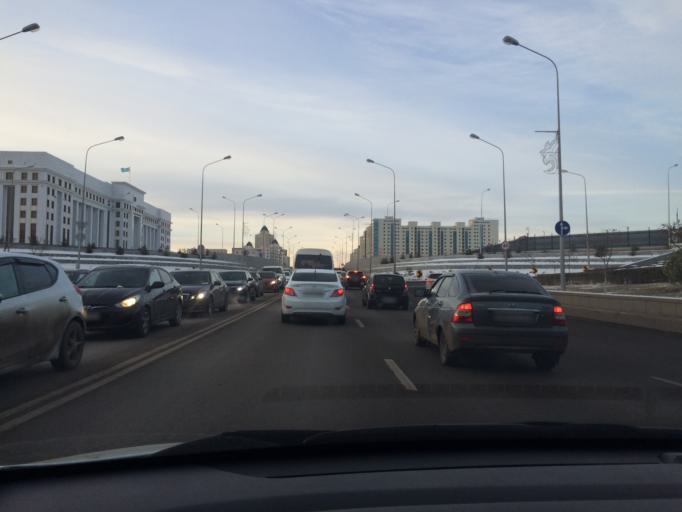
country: KZ
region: Astana Qalasy
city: Astana
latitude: 51.1219
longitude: 71.4363
